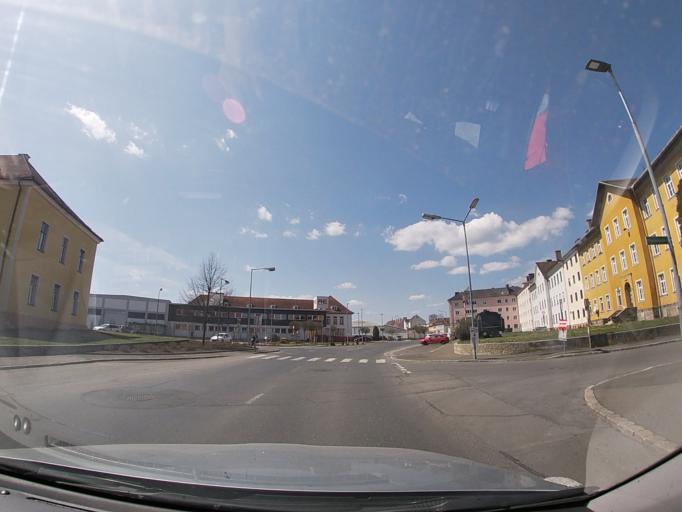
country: AT
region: Styria
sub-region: Politischer Bezirk Murtal
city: Apfelberg
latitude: 47.2162
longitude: 14.8377
